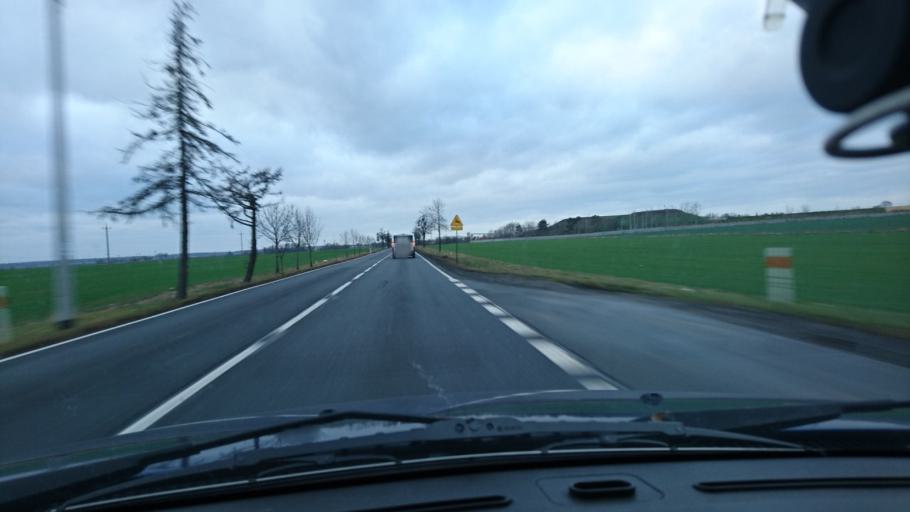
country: PL
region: Opole Voivodeship
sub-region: Powiat kluczborski
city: Kluczbork
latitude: 50.9968
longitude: 18.2080
